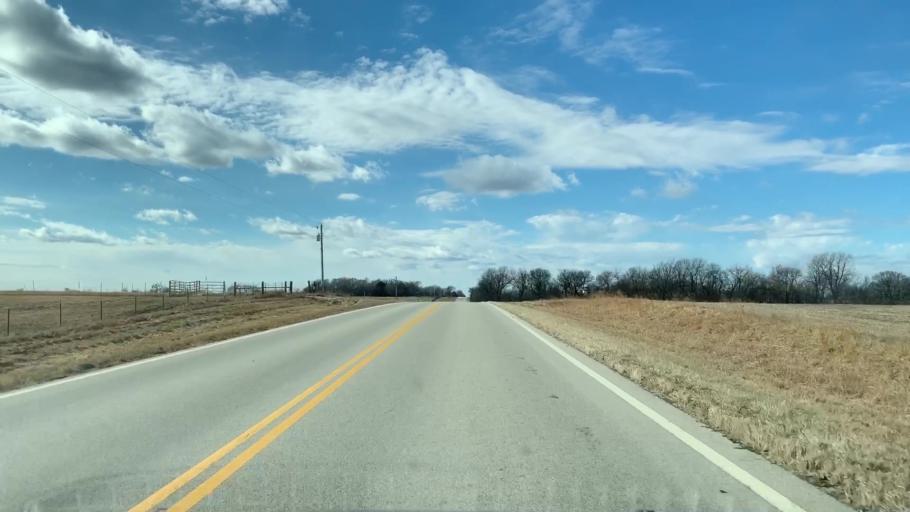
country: US
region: Kansas
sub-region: Neosho County
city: Chanute
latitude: 37.5288
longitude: -95.4351
